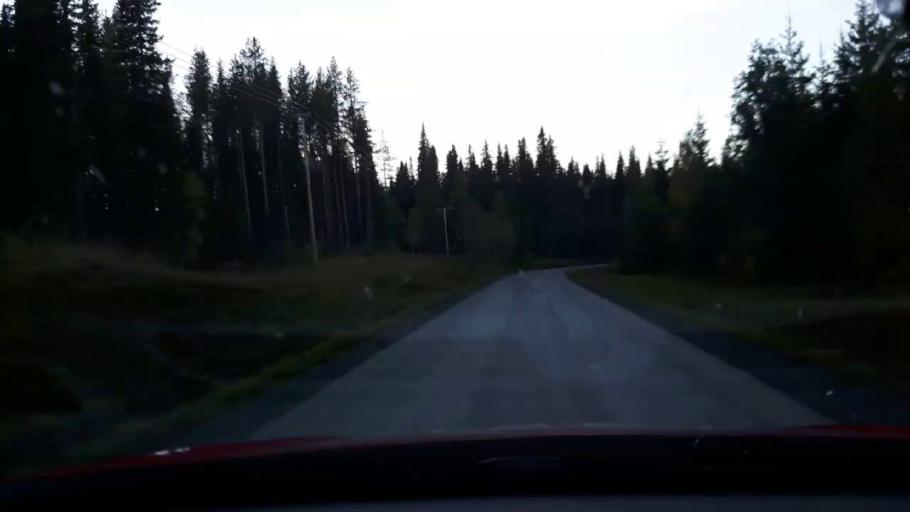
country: SE
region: Jaemtland
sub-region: Krokoms Kommun
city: Krokom
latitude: 63.4803
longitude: 14.2147
